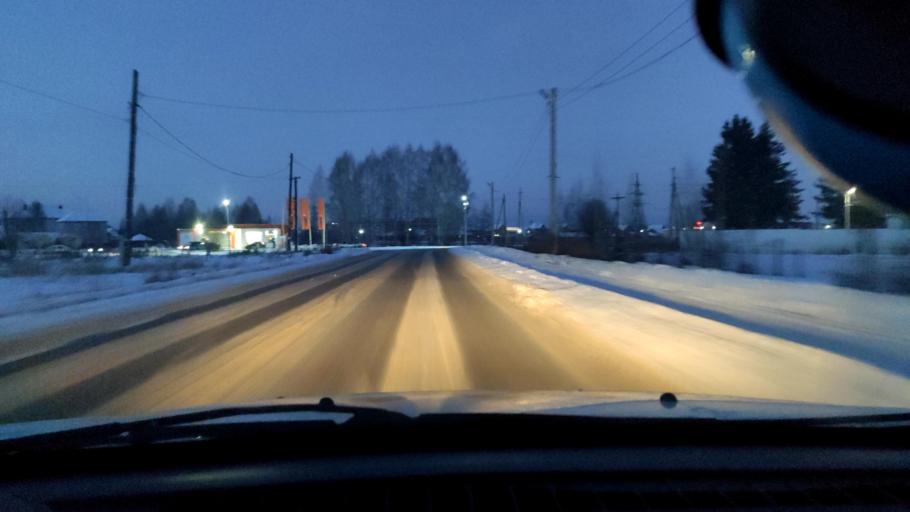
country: RU
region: Perm
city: Kultayevo
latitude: 57.8866
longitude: 55.9235
